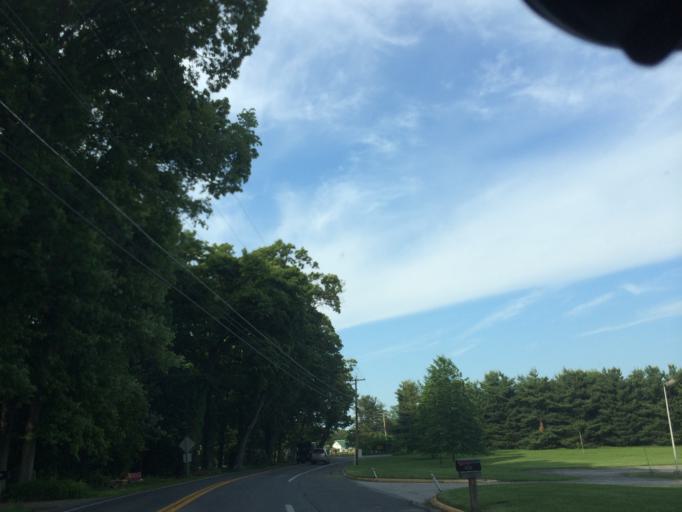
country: US
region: Maryland
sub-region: Carroll County
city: Sykesville
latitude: 39.2831
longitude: -77.0181
